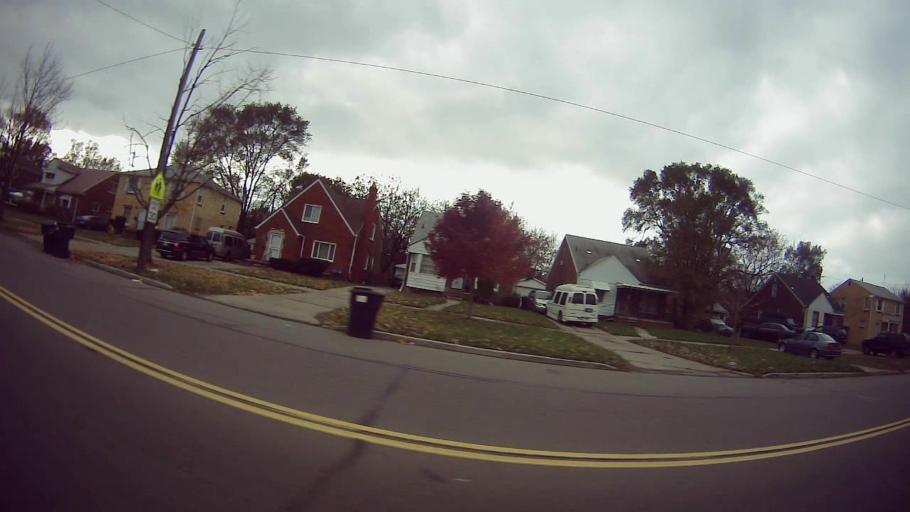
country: US
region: Michigan
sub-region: Macomb County
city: Eastpointe
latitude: 42.4470
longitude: -82.9855
